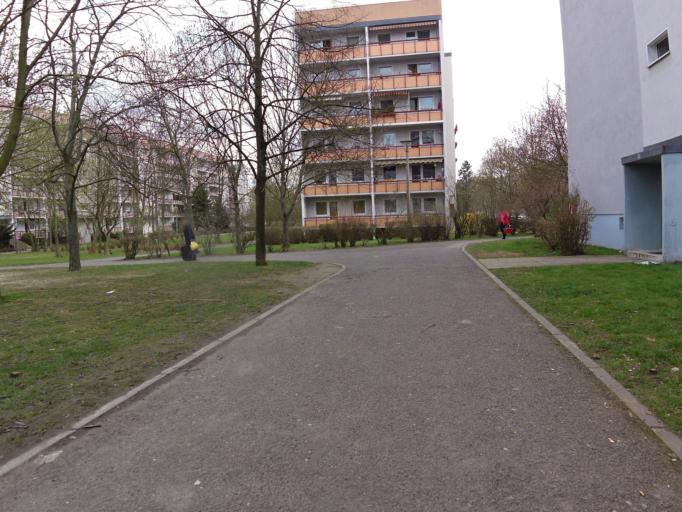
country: DE
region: Saxony
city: Markranstadt
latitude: 51.3150
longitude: 12.2949
